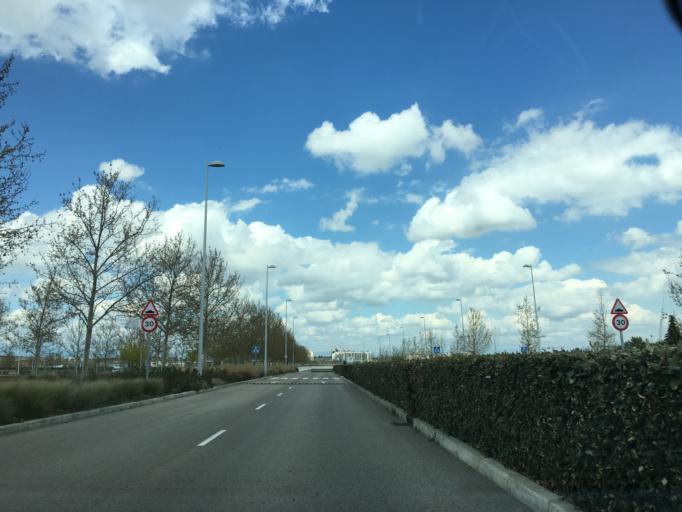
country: ES
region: Madrid
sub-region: Provincia de Madrid
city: Hortaleza
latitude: 40.4789
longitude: -3.6179
